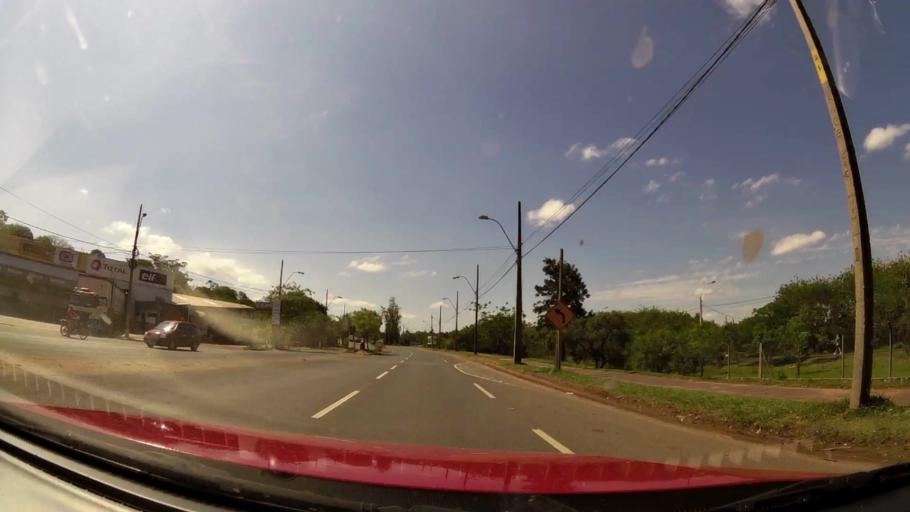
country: PY
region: Central
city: Fernando de la Mora
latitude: -25.2612
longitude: -57.5480
